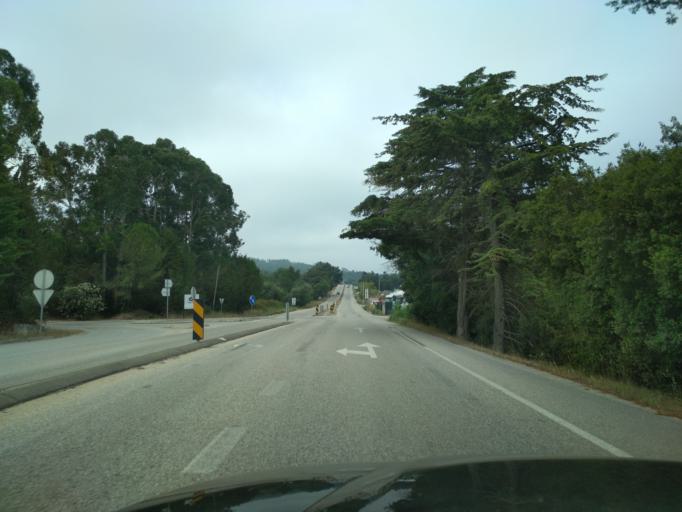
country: PT
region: Coimbra
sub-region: Condeixa-A-Nova
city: Condeixa-a-Nova
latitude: 40.0761
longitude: -8.5239
